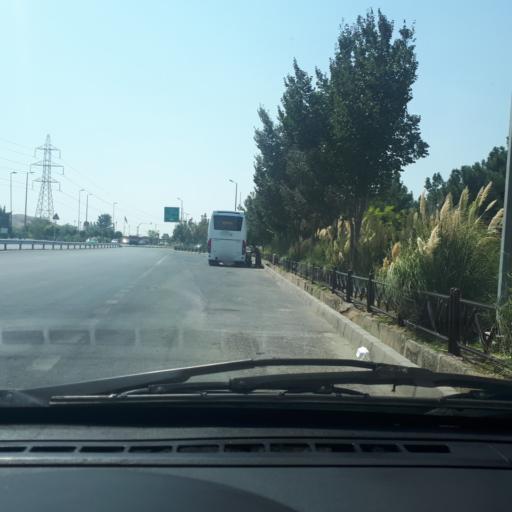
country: IR
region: Tehran
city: Tehran
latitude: 35.7038
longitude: 51.5069
